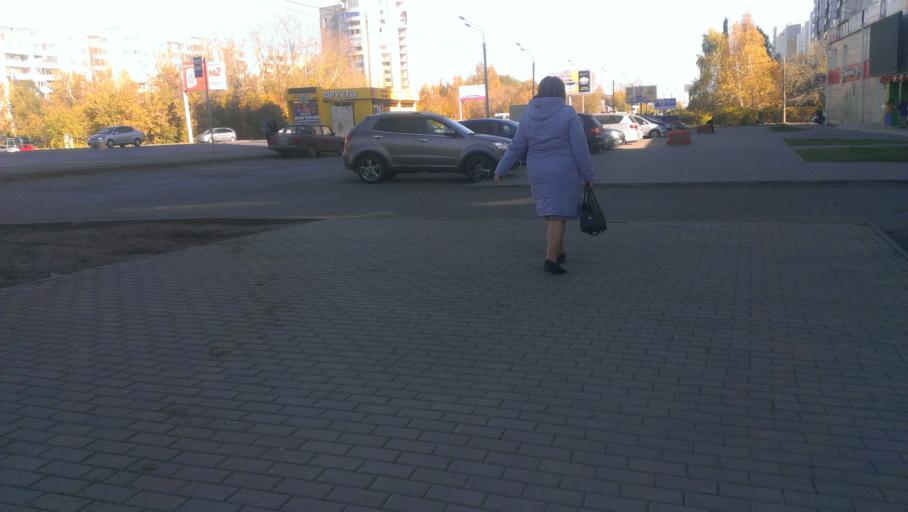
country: RU
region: Altai Krai
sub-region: Gorod Barnaulskiy
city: Barnaul
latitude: 53.3414
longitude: 83.6986
